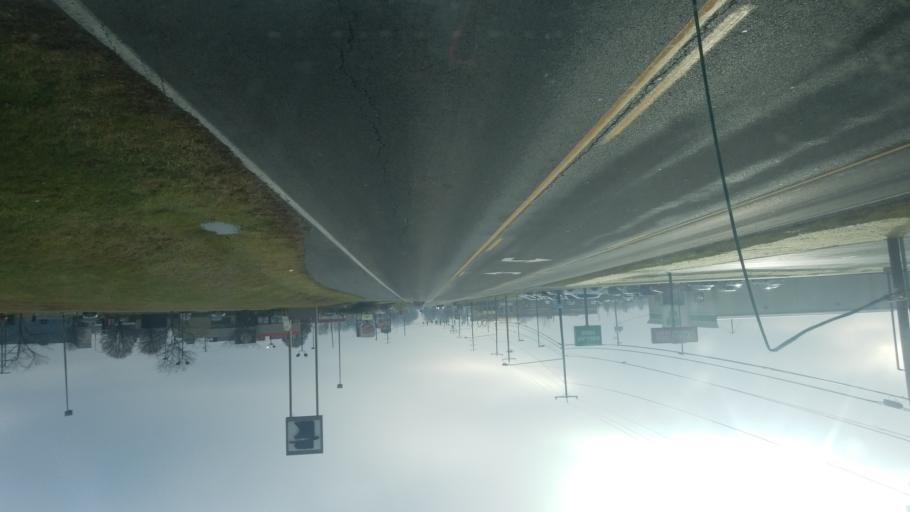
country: US
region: Ohio
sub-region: Hardin County
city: Kenton
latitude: 40.6531
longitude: -83.5883
